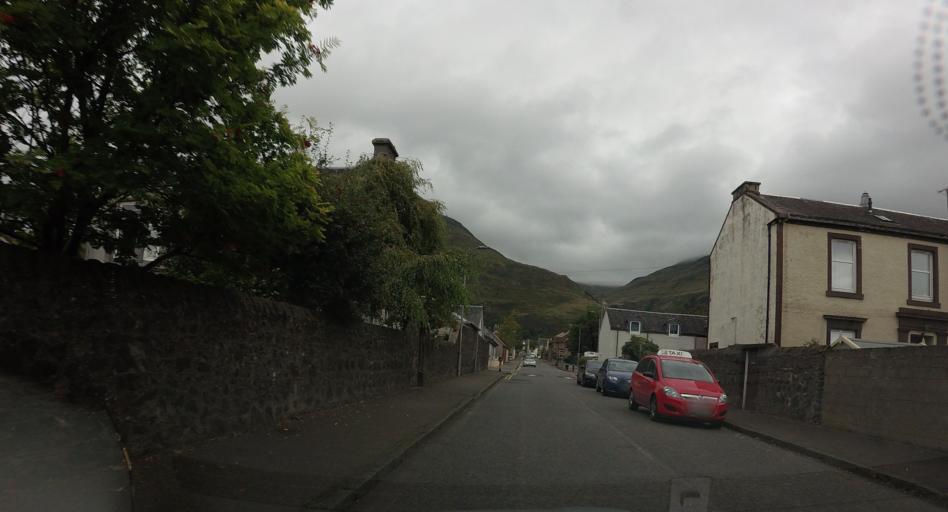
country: GB
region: Scotland
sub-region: Clackmannanshire
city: Alva
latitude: 56.1503
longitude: -3.7979
